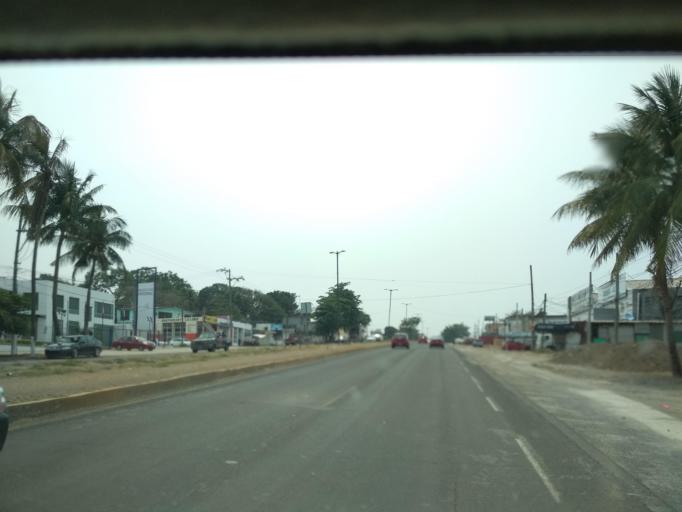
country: MX
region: Veracruz
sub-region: Veracruz
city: Las Amapolas
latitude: 19.1651
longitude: -96.2139
